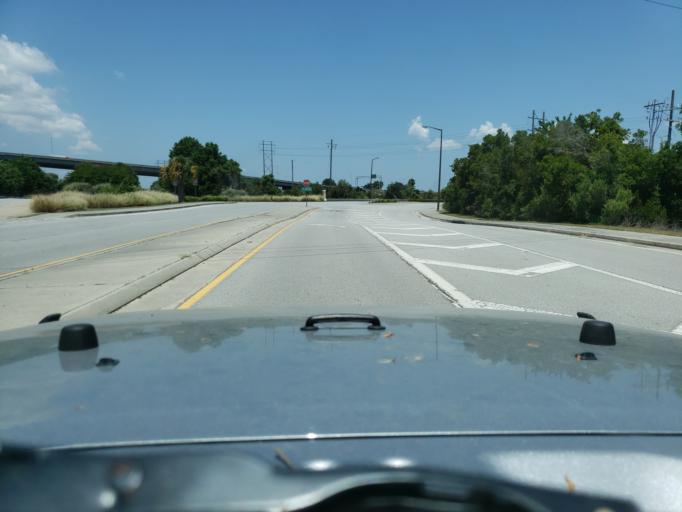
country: US
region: Georgia
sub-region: Chatham County
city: Savannah
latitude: 32.0937
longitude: -81.0911
